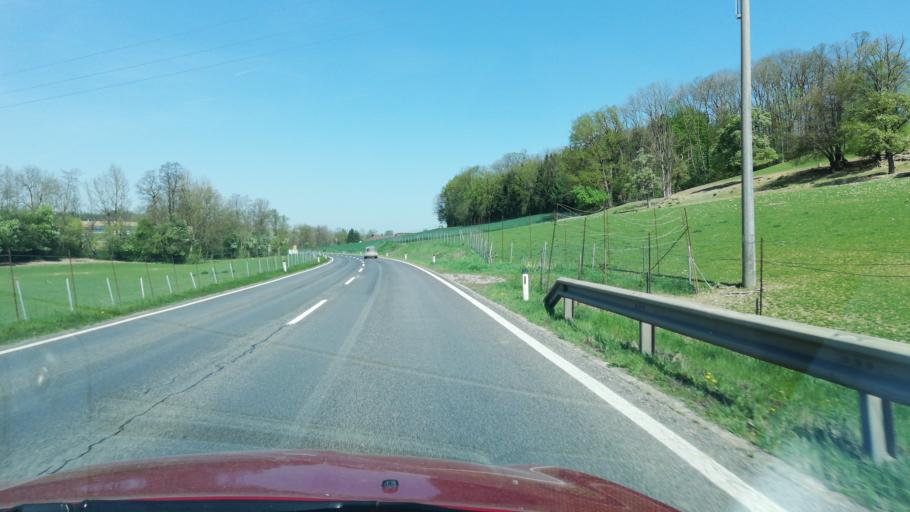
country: AT
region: Upper Austria
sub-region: Wels-Land
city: Thalheim bei Wels
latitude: 48.1310
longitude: 14.0516
